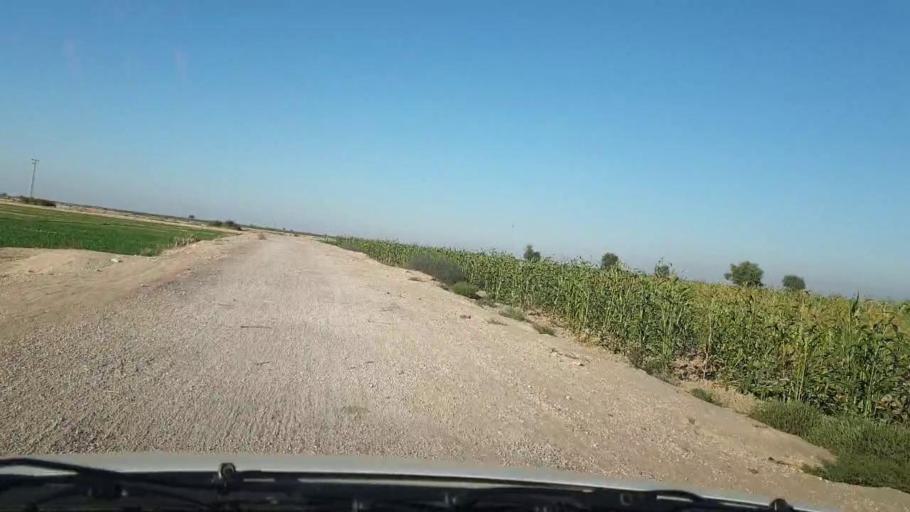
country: PK
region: Sindh
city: Johi
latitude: 26.7398
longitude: 67.5033
